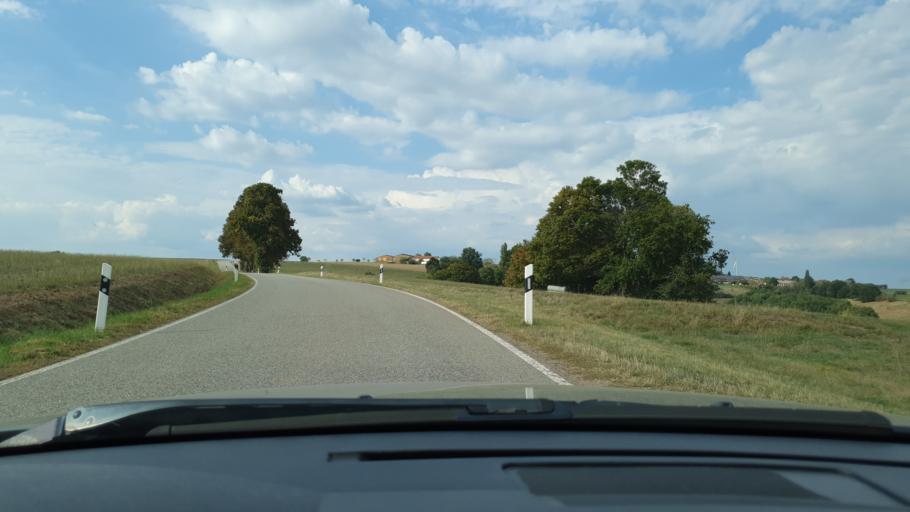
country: DE
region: Rheinland-Pfalz
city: Gerhardsbrunn
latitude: 49.3449
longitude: 7.5220
